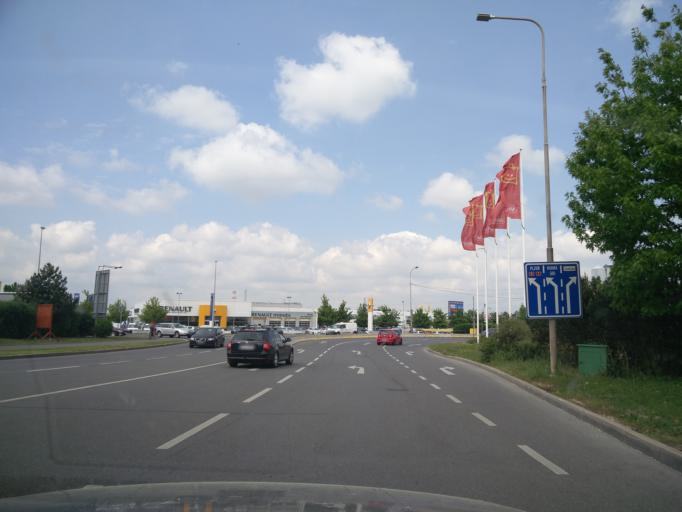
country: CZ
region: Central Bohemia
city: Hostivice
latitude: 50.0501
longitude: 14.2939
